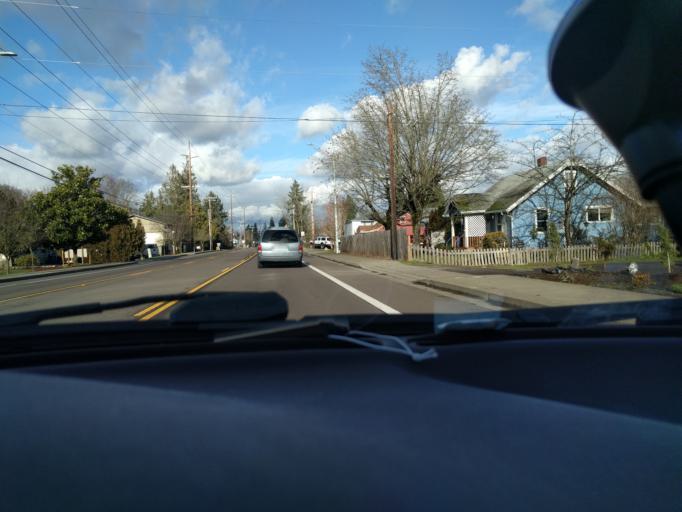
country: US
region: Oregon
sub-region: Marion County
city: Hayesville
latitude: 44.9714
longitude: -122.9916
